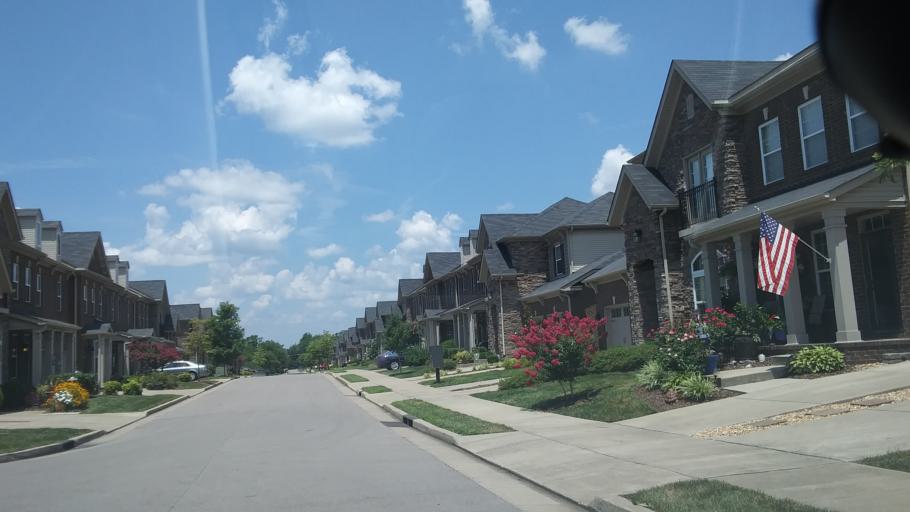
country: US
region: Tennessee
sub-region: Davidson County
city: Belle Meade
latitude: 36.1187
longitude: -86.9238
